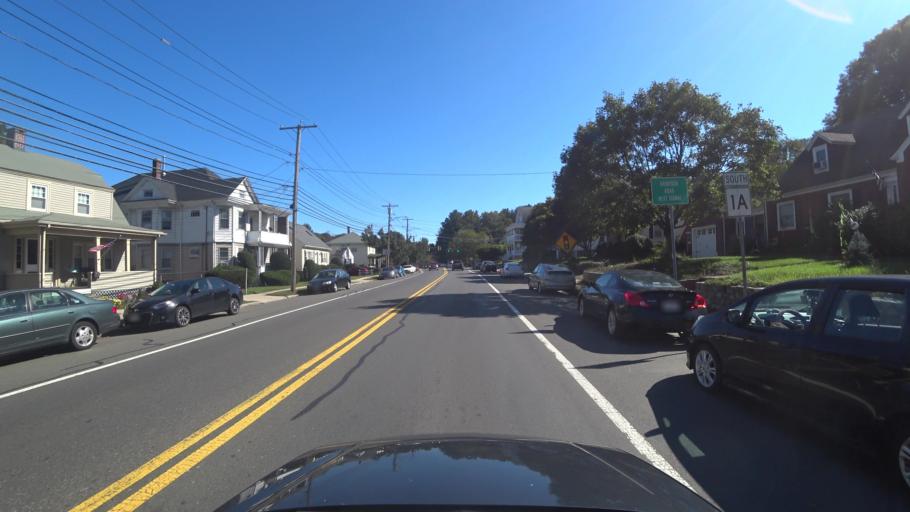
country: US
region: Massachusetts
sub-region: Essex County
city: Salem
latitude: 42.4952
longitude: -70.8947
